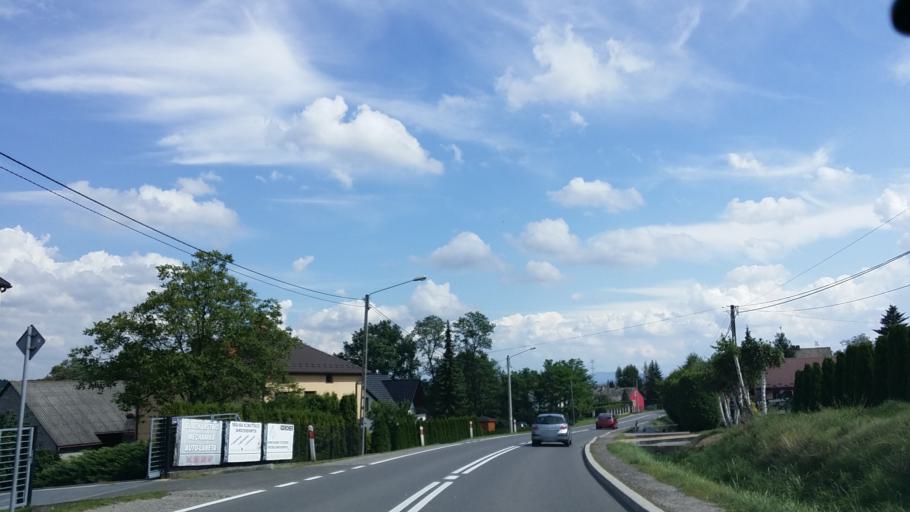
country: PL
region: Lesser Poland Voivodeship
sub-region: Powiat myslenicki
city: Dobczyce
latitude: 49.9180
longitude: 20.0872
